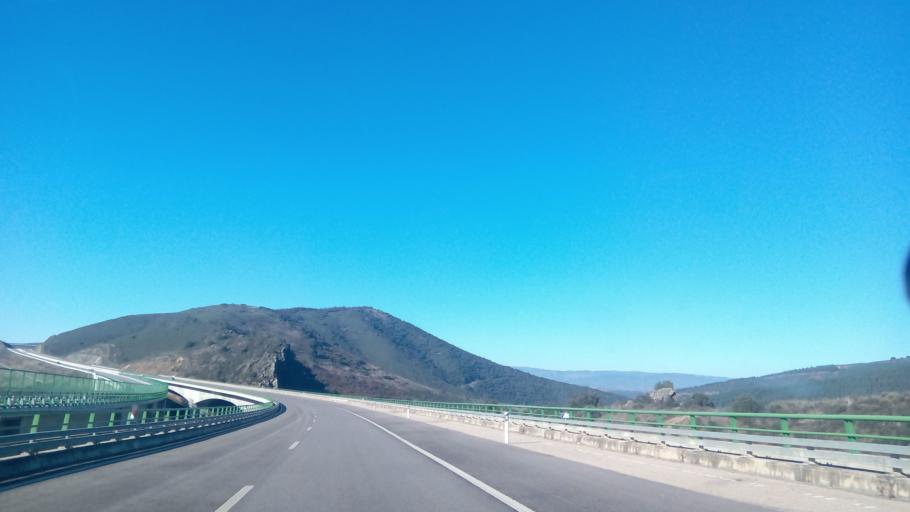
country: PT
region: Braganca
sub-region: Braganca Municipality
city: Braganca
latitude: 41.7746
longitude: -6.6750
